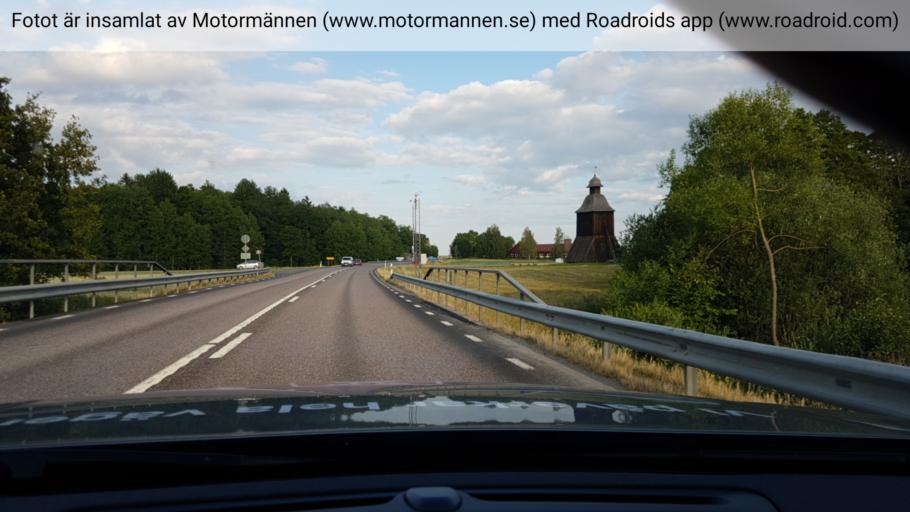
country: SE
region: Uppsala
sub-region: Enkopings Kommun
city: Orsundsbro
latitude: 59.8782
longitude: 17.2835
